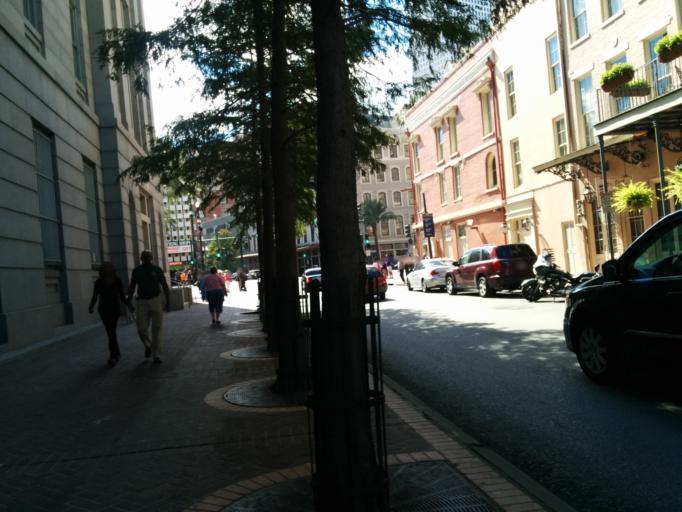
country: US
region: Louisiana
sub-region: Orleans Parish
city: New Orleans
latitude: 29.9524
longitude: -90.0668
